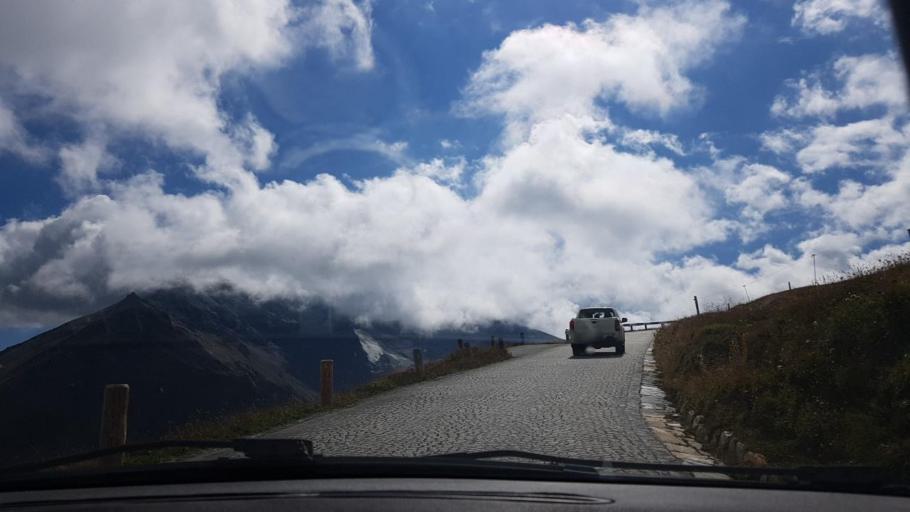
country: AT
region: Carinthia
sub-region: Politischer Bezirk Spittal an der Drau
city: Heiligenblut
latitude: 47.1204
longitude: 12.8316
